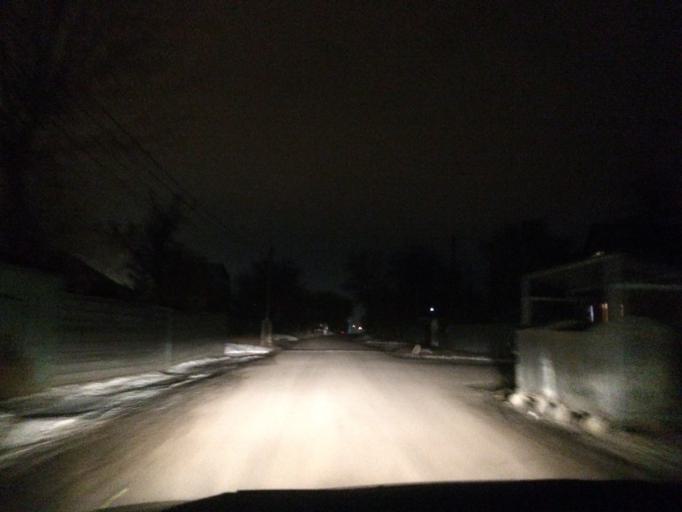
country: KZ
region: Astana Qalasy
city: Astana
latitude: 51.2094
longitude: 71.3920
